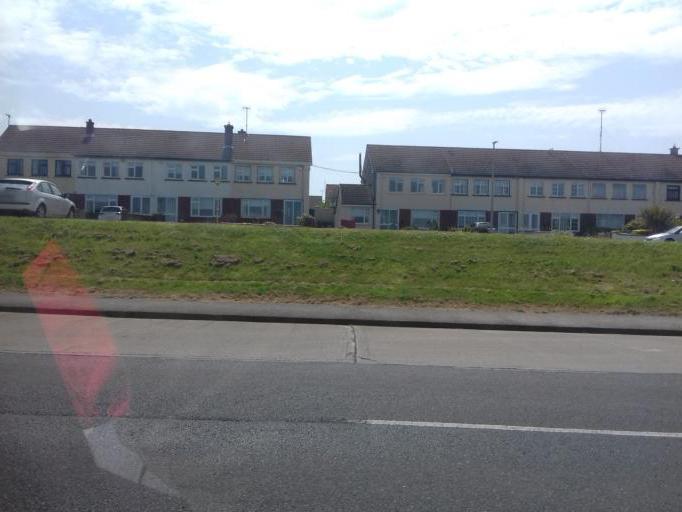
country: IE
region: Leinster
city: Portraine
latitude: 53.4932
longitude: -6.1067
